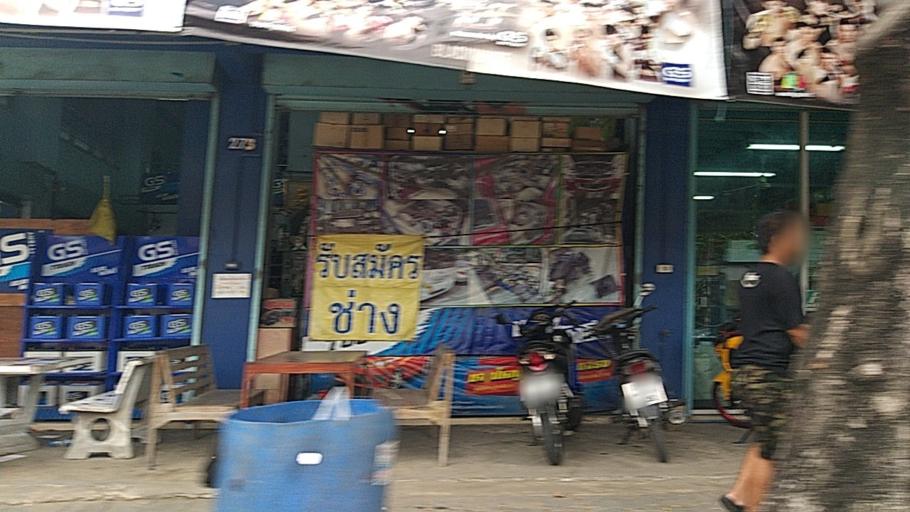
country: TH
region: Bangkok
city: Bang Na
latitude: 13.6794
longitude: 100.6637
